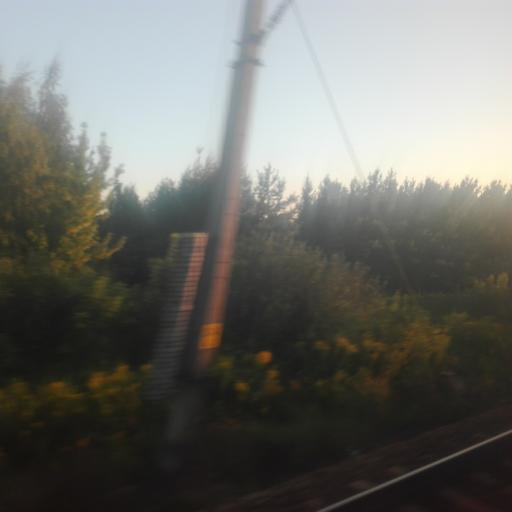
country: PL
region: Masovian Voivodeship
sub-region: Powiat warszawski zachodni
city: Bieniewice
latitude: 52.1896
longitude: 20.5302
